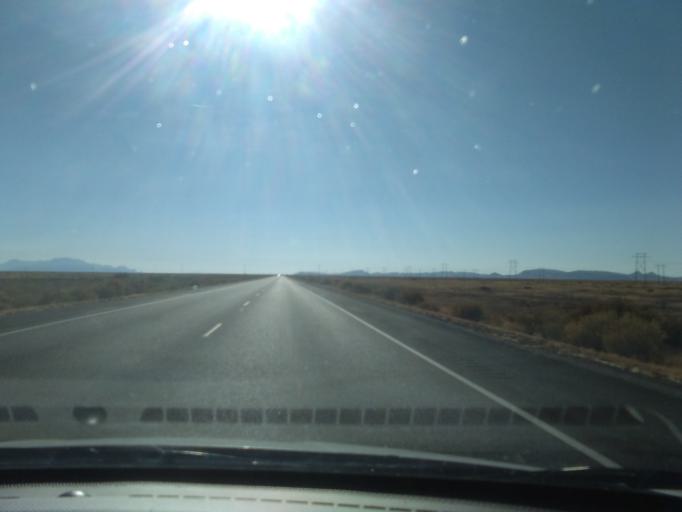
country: US
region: New Mexico
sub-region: Luna County
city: Deming
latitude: 32.5218
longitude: -107.4963
